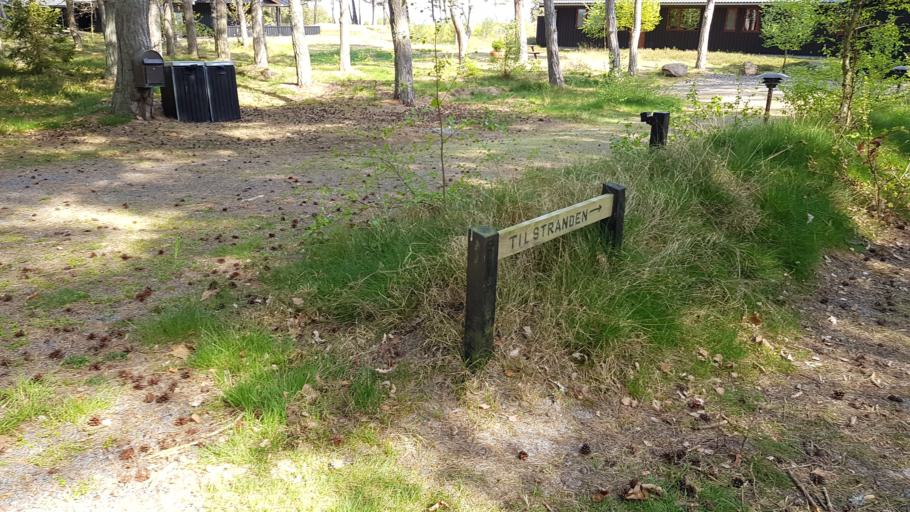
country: DK
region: Capital Region
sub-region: Bornholm Kommune
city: Nexo
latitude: 55.0012
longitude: 15.0941
